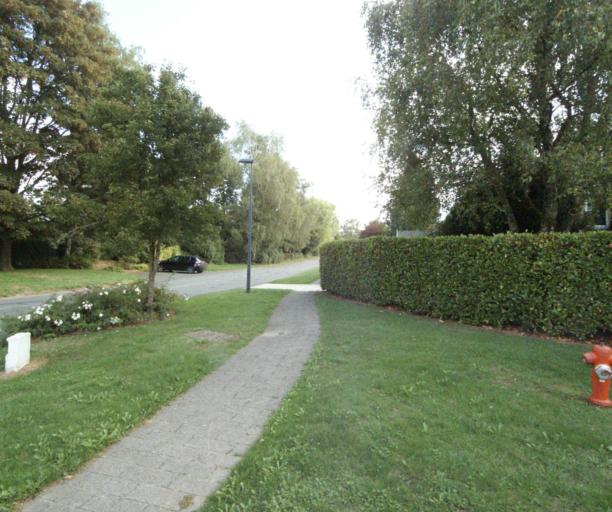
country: FR
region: Nord-Pas-de-Calais
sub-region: Departement du Nord
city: Villeneuve-d'Ascq
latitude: 50.6288
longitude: 3.1566
